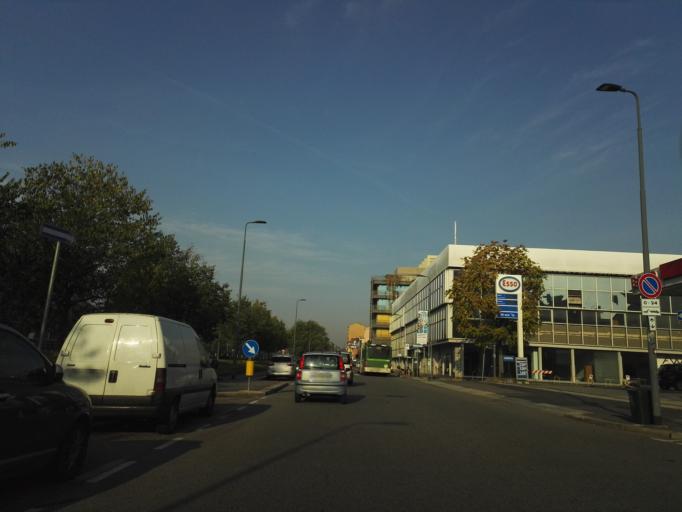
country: IT
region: Lombardy
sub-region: Citta metropolitana di Milano
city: Chiaravalle
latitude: 45.4359
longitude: 9.2331
